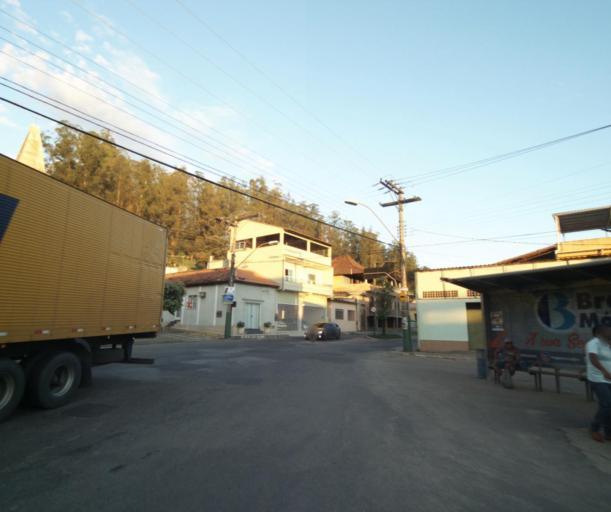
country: BR
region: Rio de Janeiro
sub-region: Bom Jesus Do Itabapoana
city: Bom Jesus do Itabapoana
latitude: -21.1570
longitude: -41.5647
